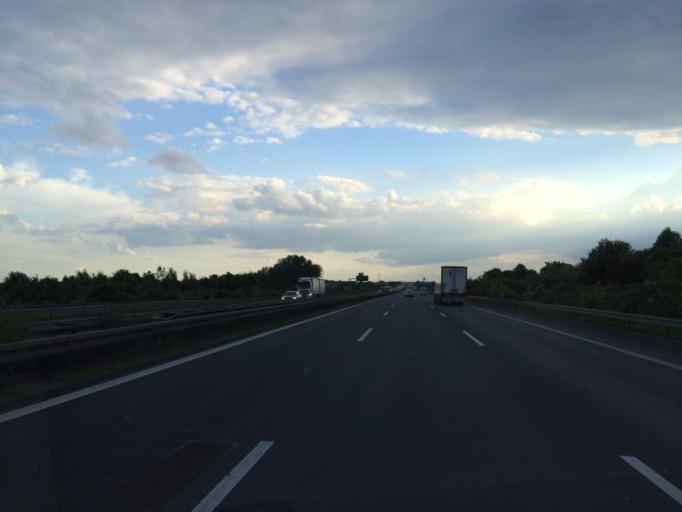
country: DE
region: Saxony-Anhalt
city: Glindenberg
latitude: 52.2107
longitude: 11.6637
